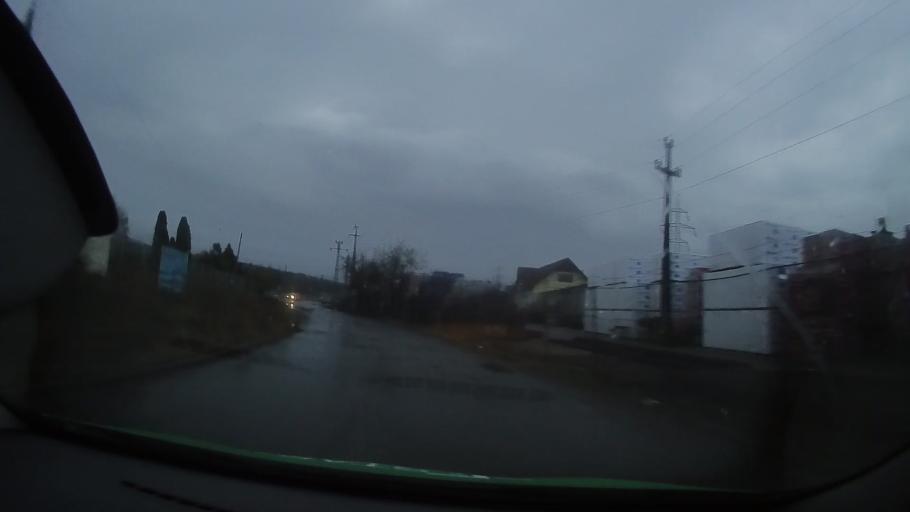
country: RO
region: Mures
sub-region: Municipiul Reghin
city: Iernuteni
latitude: 46.7668
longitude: 24.7223
